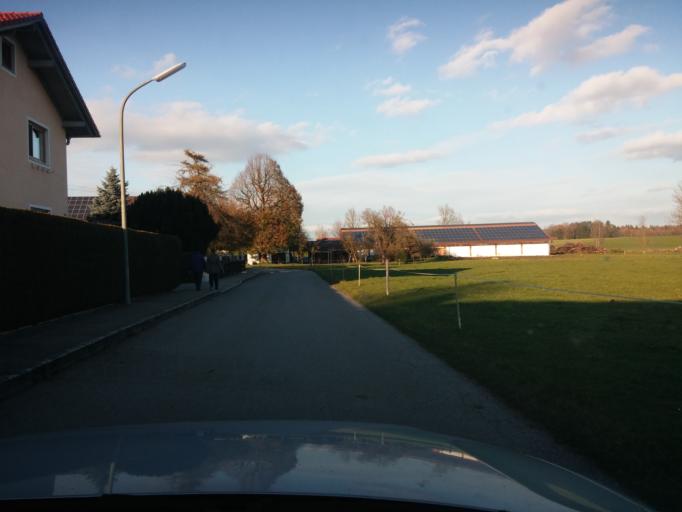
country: DE
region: Bavaria
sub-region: Upper Bavaria
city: Bad Aibling
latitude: 47.8776
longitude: 11.9983
